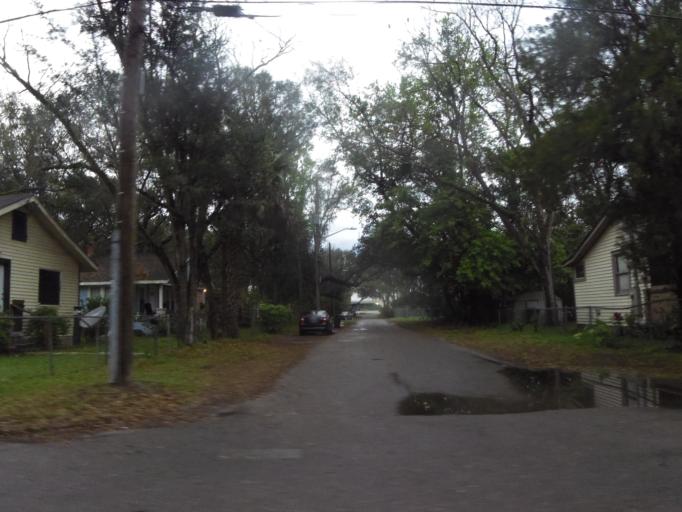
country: US
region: Florida
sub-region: Duval County
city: Jacksonville
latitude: 30.3278
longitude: -81.7022
